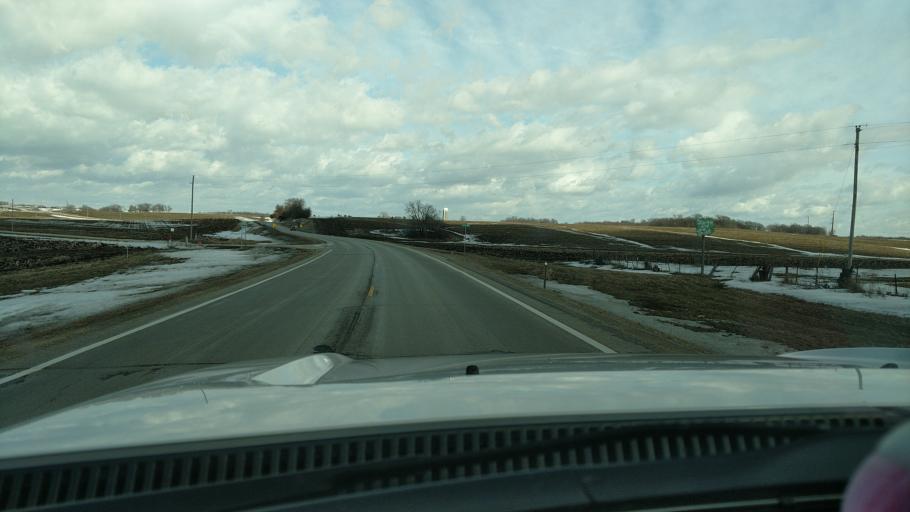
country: US
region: Minnesota
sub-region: Wabasha County
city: Plainview
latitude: 44.1882
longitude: -92.1407
